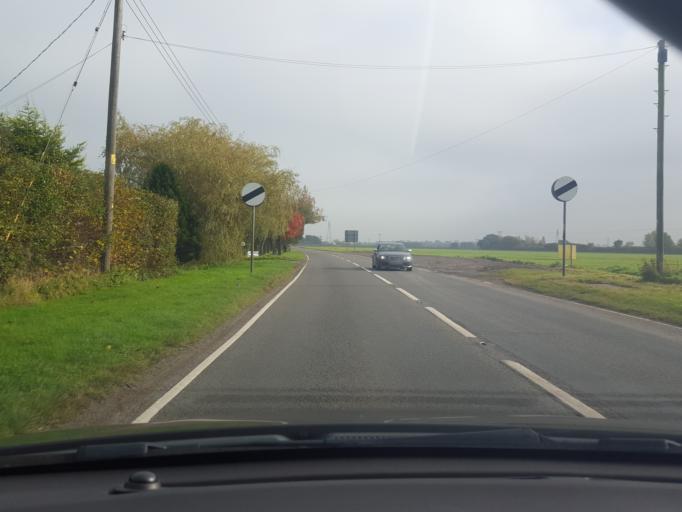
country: GB
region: England
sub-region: Suffolk
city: East Bergholt
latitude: 51.9367
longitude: 1.0133
